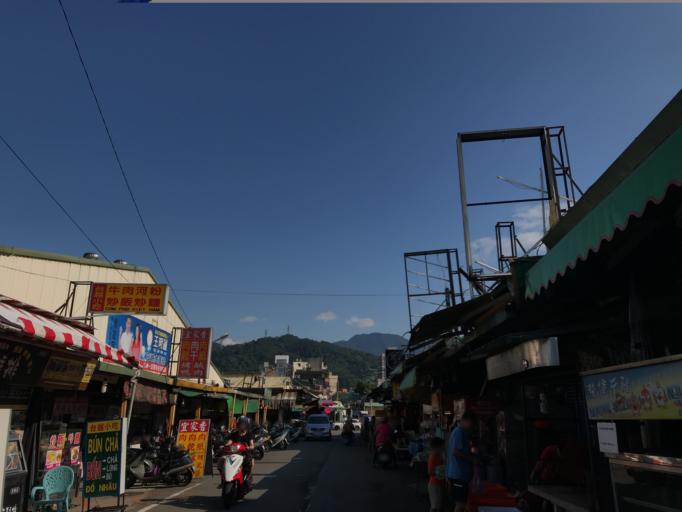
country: TW
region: Taiwan
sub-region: Taoyuan
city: Taoyuan
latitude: 24.9334
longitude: 121.3744
